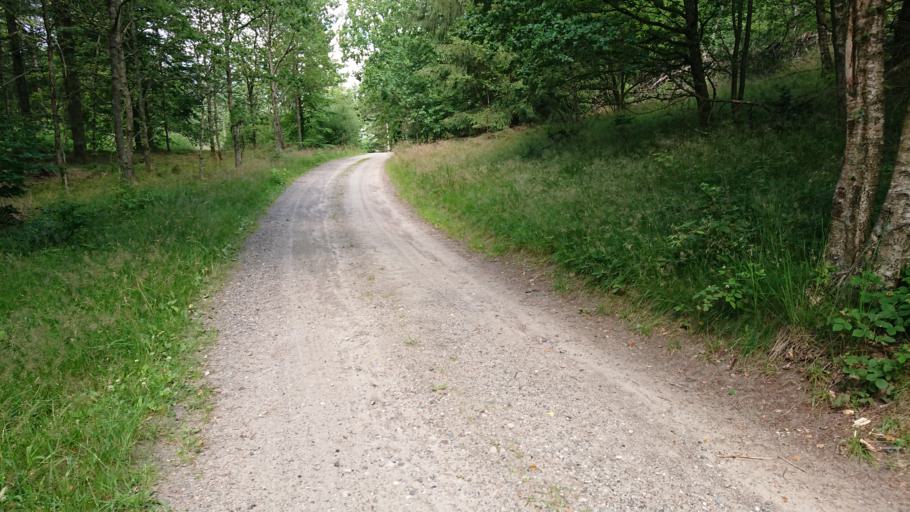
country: DK
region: North Denmark
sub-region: Hjorring Kommune
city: Sindal
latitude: 57.4471
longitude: 10.3478
